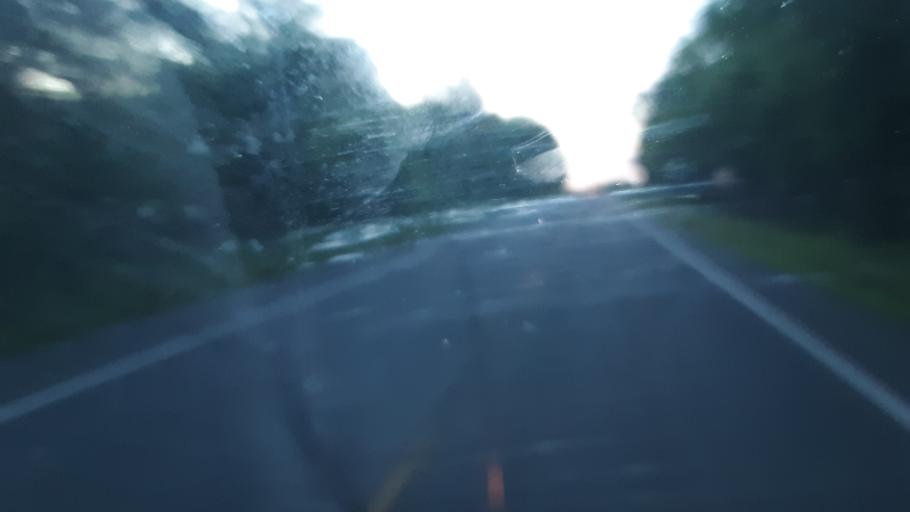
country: US
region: New York
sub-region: Montgomery County
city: Hagaman
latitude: 42.9754
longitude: -74.0564
